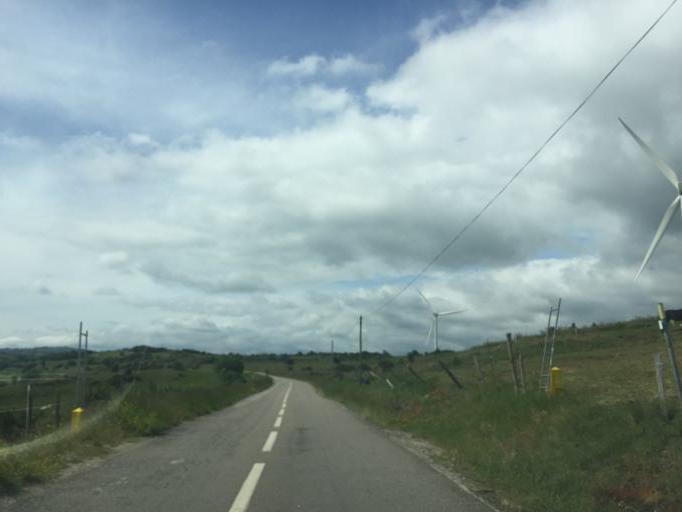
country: FR
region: Rhone-Alpes
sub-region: Departement de l'Ardeche
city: Saint-Priest
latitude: 44.6761
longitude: 4.5566
